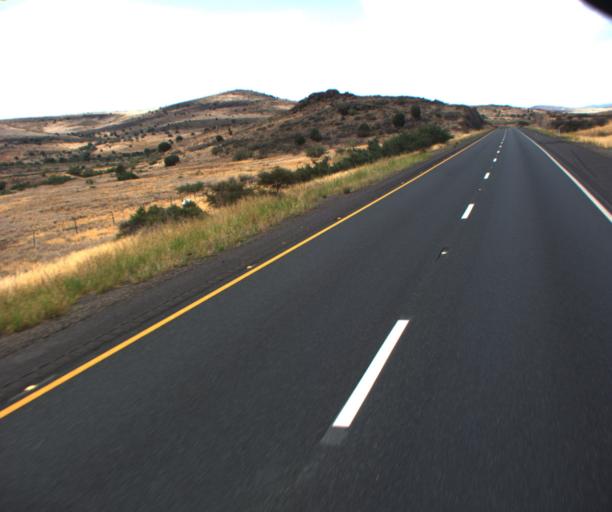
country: US
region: Arizona
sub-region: Yavapai County
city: Cordes Lakes
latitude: 34.4753
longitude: -112.0241
